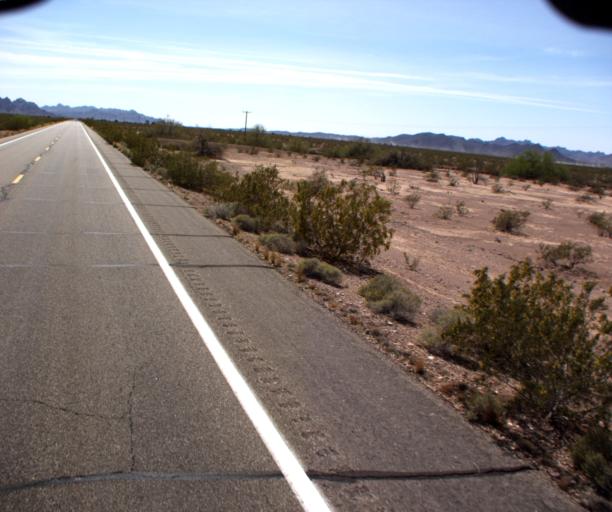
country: US
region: Arizona
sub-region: La Paz County
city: Quartzsite
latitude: 33.3655
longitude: -114.2171
